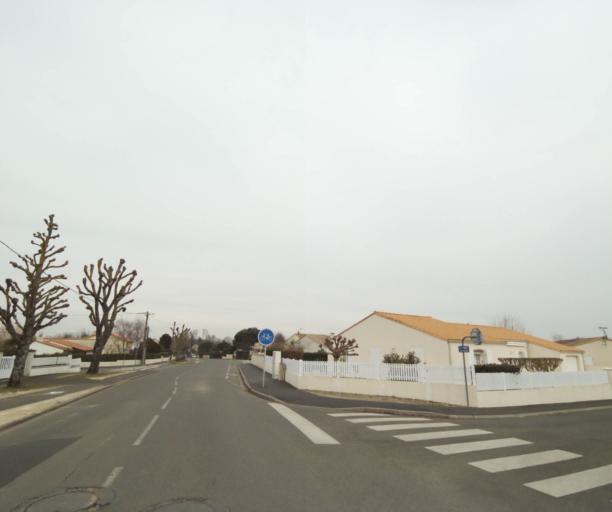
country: FR
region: Poitou-Charentes
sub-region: Departement des Deux-Sevres
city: Bessines
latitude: 46.3194
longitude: -0.5151
